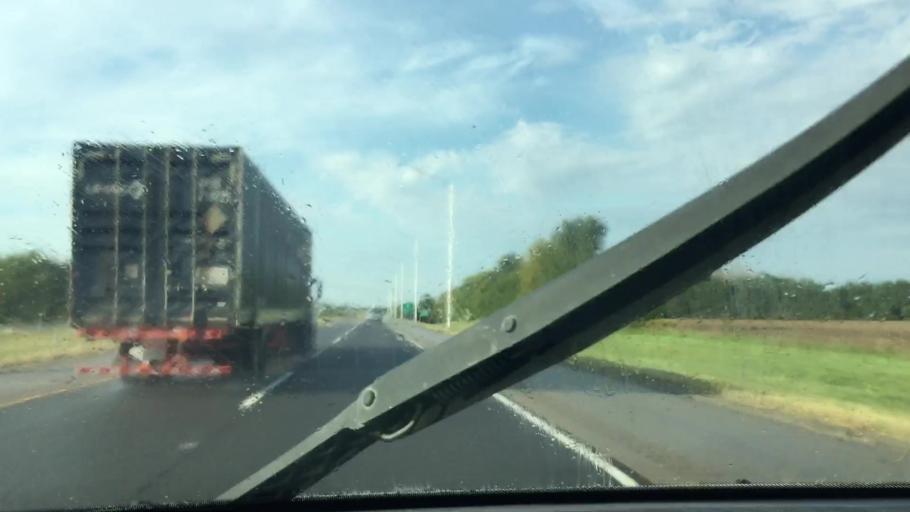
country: US
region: Illinois
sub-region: Whiteside County
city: Rock Falls
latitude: 41.7639
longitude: -89.6303
